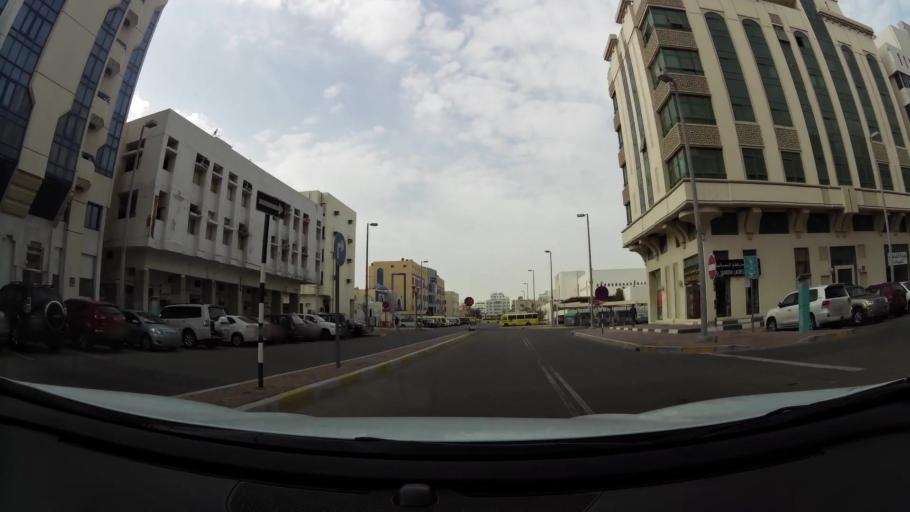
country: AE
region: Abu Dhabi
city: Abu Dhabi
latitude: 24.4598
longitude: 54.3877
